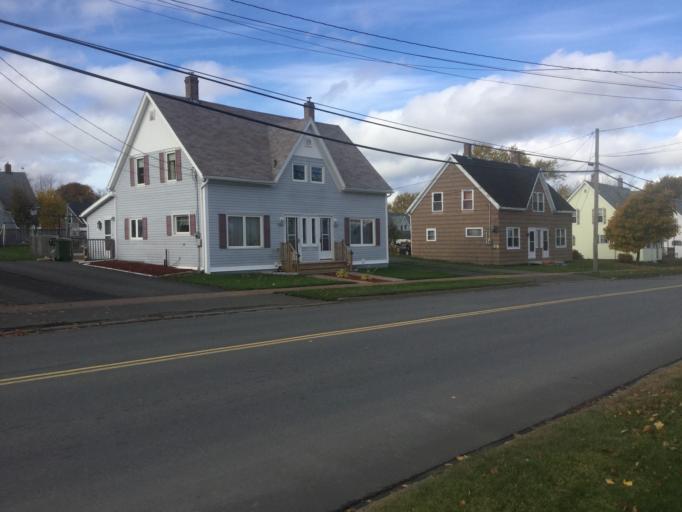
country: CA
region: Nova Scotia
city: New Glasgow
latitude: 45.5638
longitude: -62.6595
